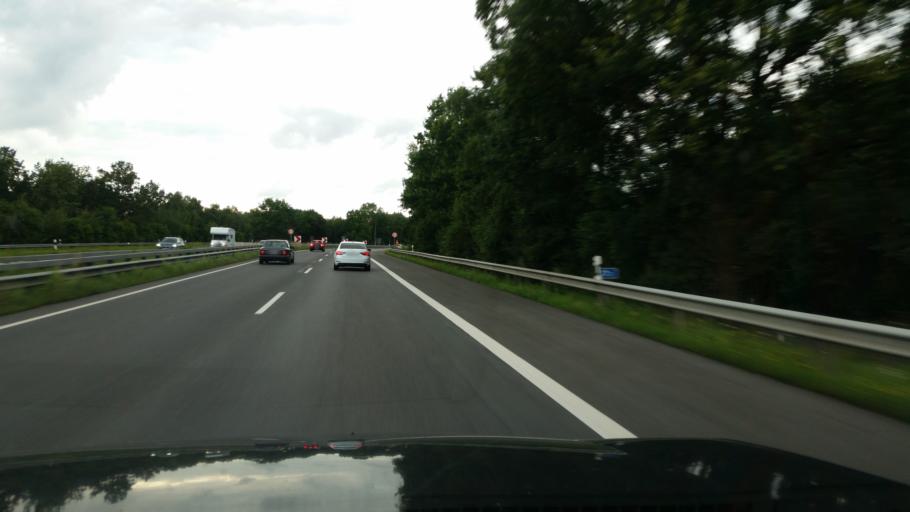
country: DE
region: Lower Saxony
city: Harmstorf
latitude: 53.3783
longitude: 10.0186
